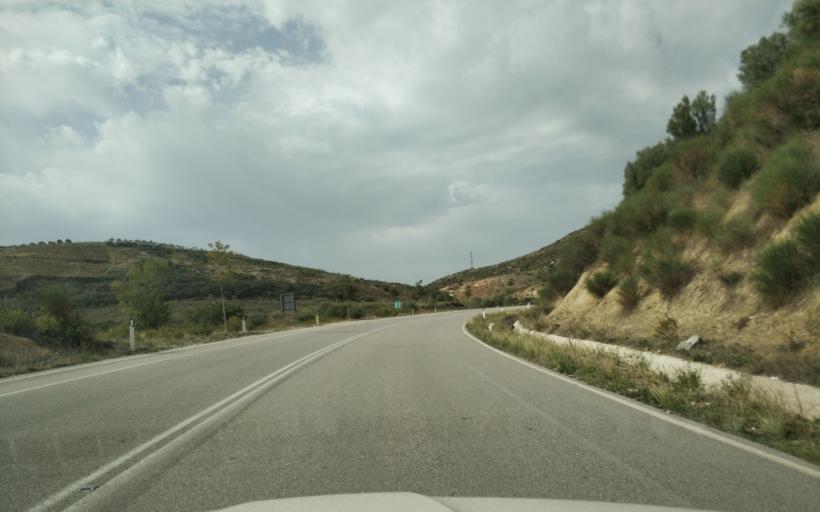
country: AL
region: Gjirokaster
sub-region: Rrethi i Tepelenes
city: Krahes
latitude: 40.3938
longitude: 19.8727
